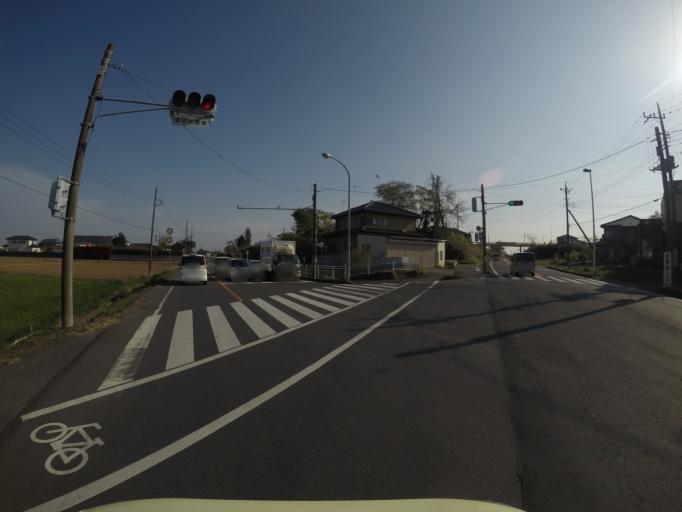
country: JP
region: Ibaraki
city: Ishige
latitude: 36.1997
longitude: 139.9749
